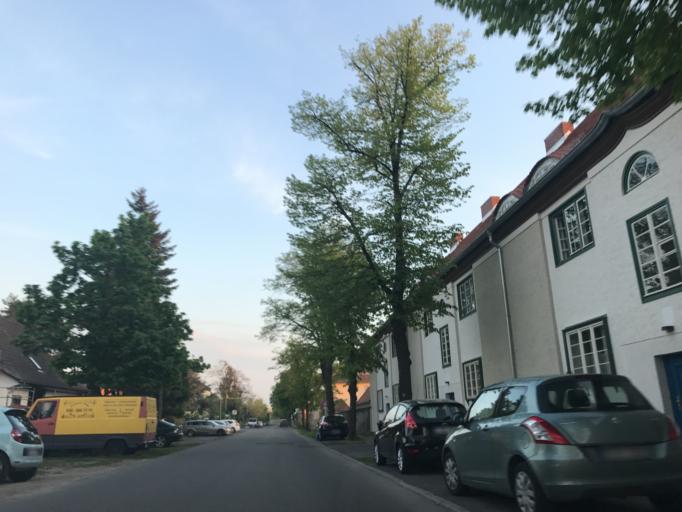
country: DE
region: Berlin
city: Staaken
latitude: 52.5407
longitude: 13.1503
